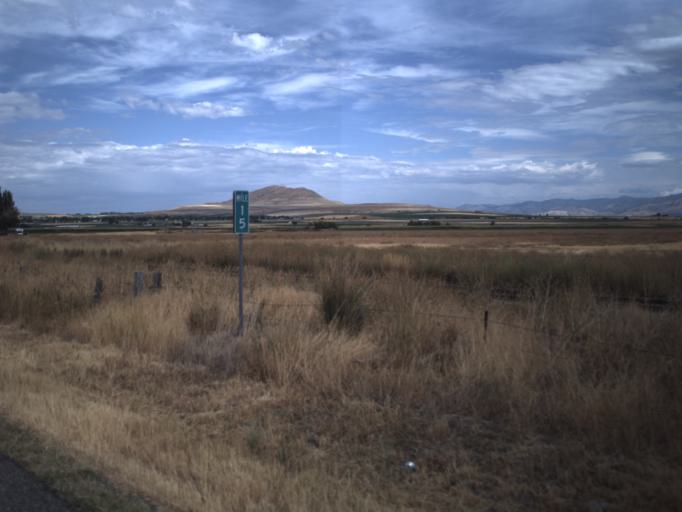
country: US
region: Utah
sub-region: Cache County
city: Benson
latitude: 41.8199
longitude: -111.9981
